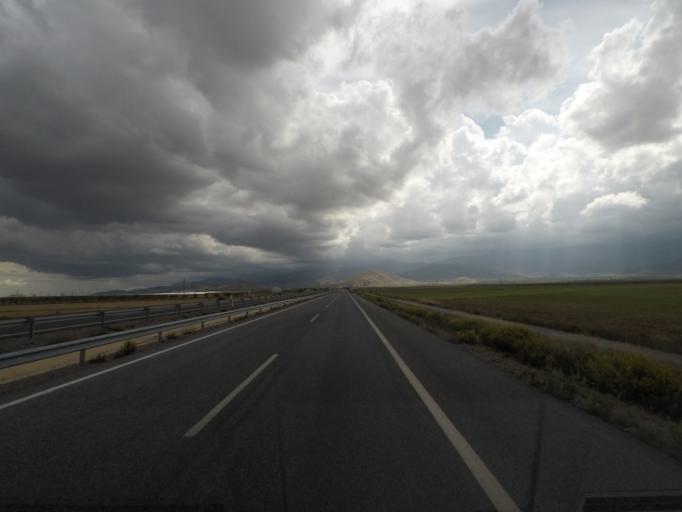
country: ES
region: Andalusia
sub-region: Provincia de Granada
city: Albunan
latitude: 37.2218
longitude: -3.0776
